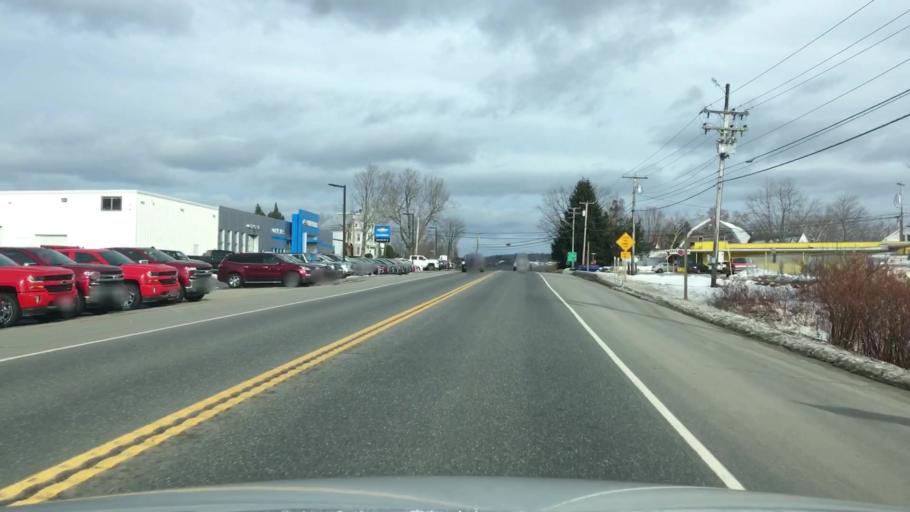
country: US
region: Maine
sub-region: Kennebec County
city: Winthrop
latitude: 44.2954
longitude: -69.9861
